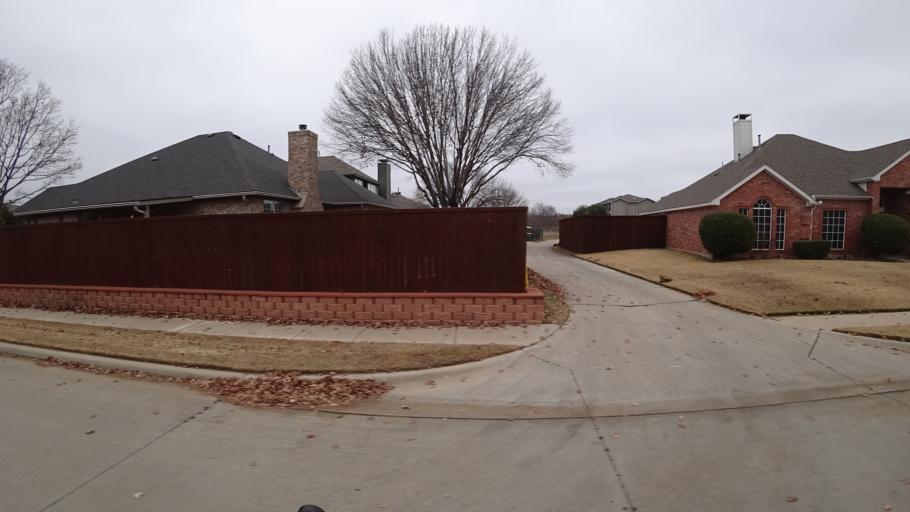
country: US
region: Texas
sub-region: Denton County
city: Highland Village
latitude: 33.0599
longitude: -97.0336
